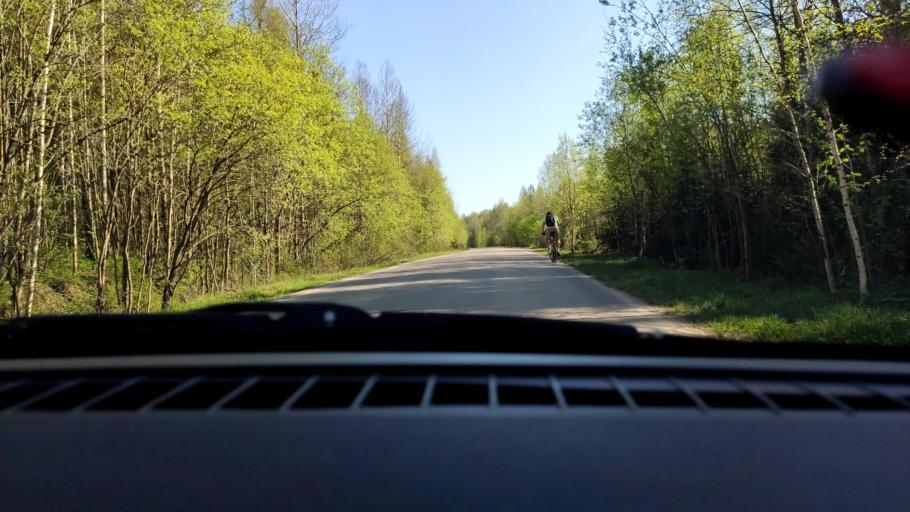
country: RU
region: Perm
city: Overyata
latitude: 58.0738
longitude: 56.0015
